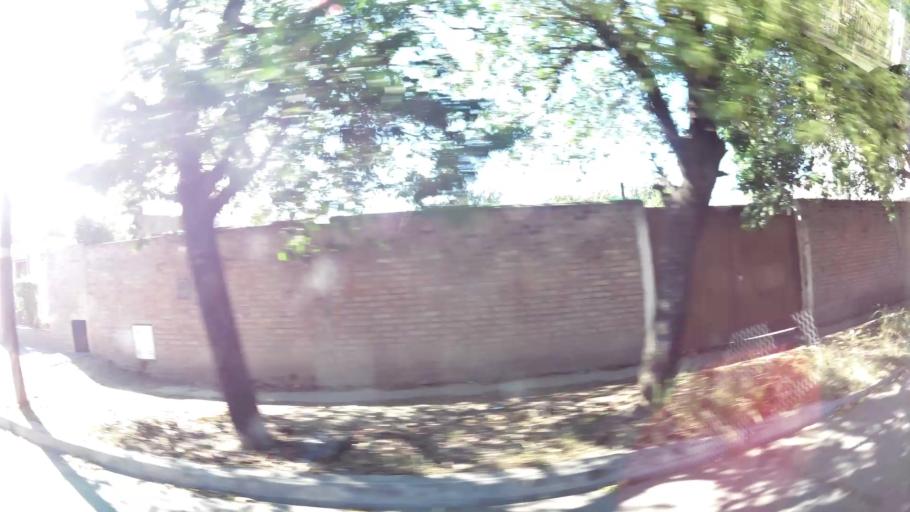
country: AR
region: Cordoba
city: Villa Allende
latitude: -31.3471
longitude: -64.2437
